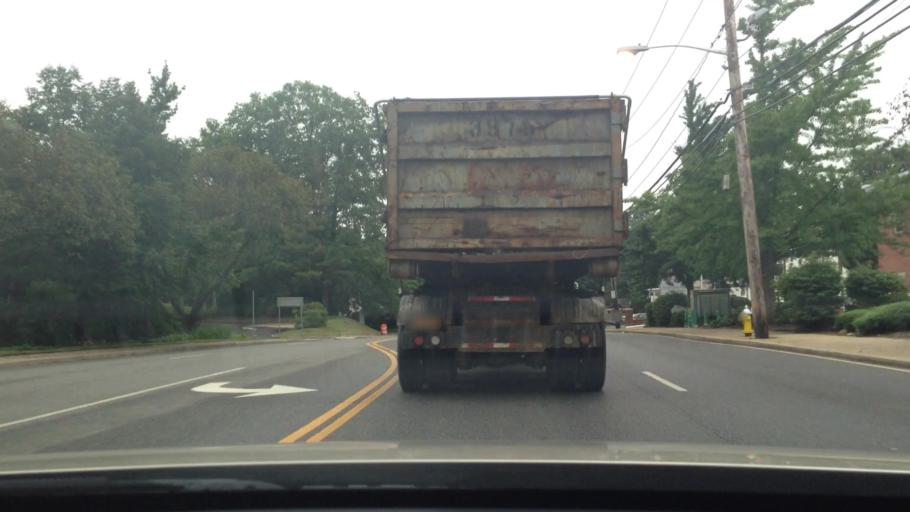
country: US
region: New York
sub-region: Nassau County
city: Thomaston
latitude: 40.7812
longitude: -73.7164
